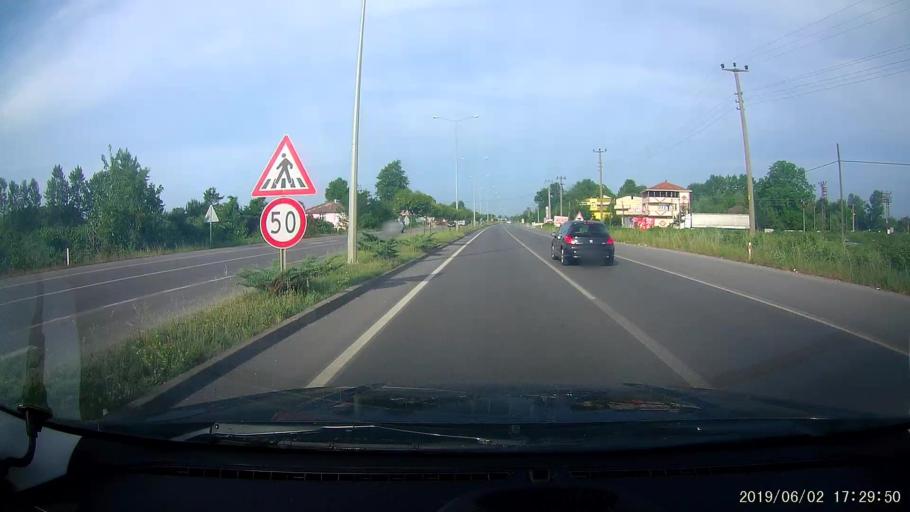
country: TR
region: Samsun
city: Carsamba
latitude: 41.2134
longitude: 36.7675
